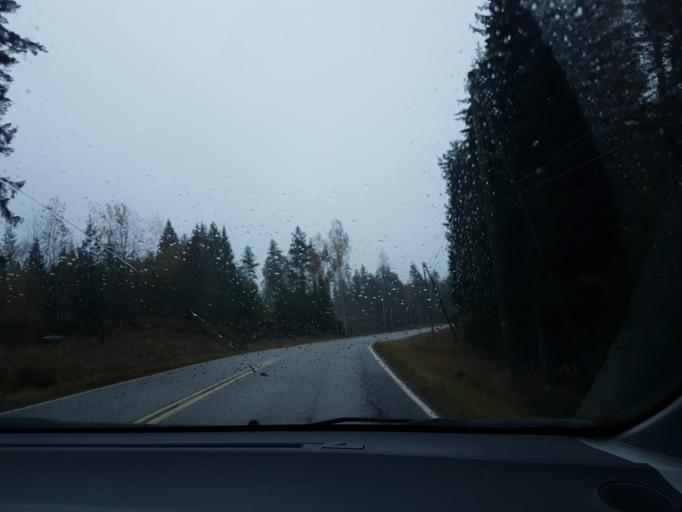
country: FI
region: Uusimaa
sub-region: Helsinki
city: Jaervenpaeae
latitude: 60.5812
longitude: 25.1657
